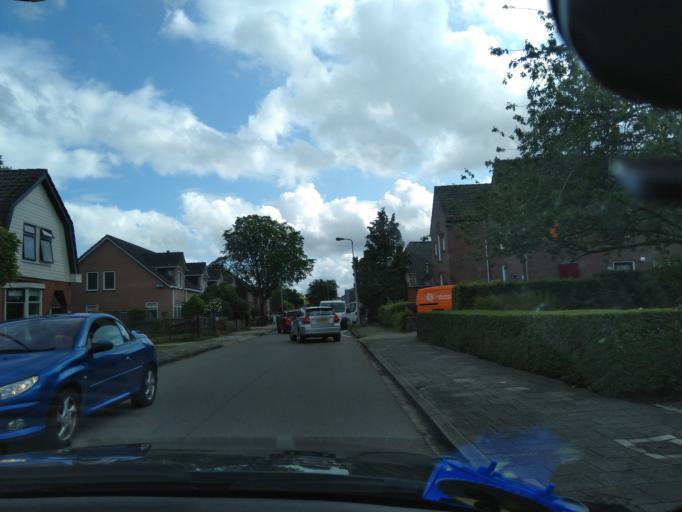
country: NL
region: Groningen
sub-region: Gemeente Zuidhorn
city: Aduard
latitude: 53.2205
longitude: 6.5003
